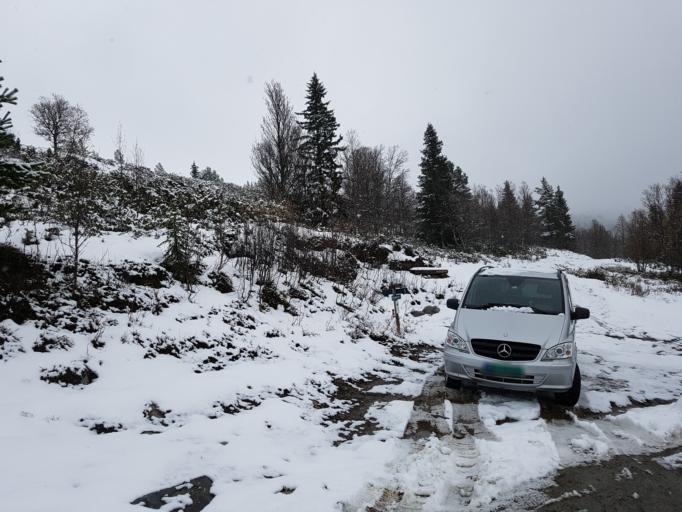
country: NO
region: Oppland
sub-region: Sel
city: Otta
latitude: 61.7972
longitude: 9.7143
